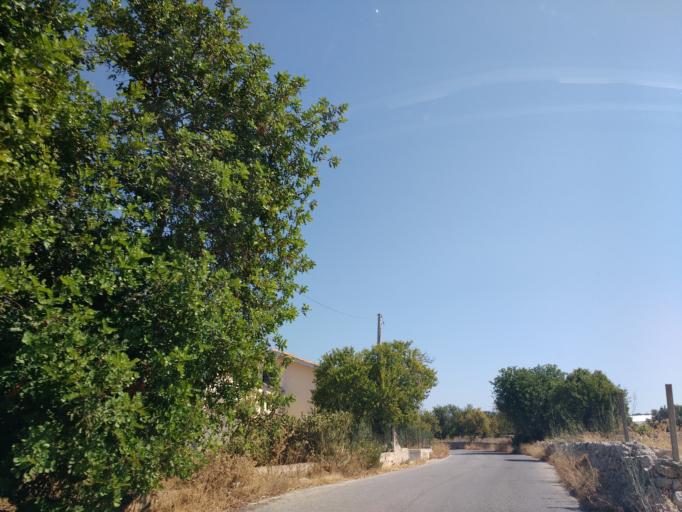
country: IT
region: Sicily
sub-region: Ragusa
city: Scicli
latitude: 36.7599
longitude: 14.7039
